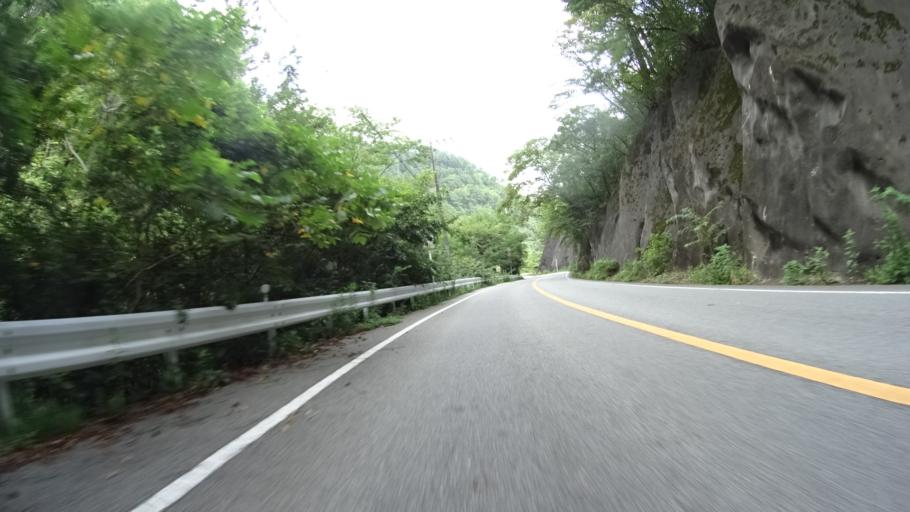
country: JP
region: Yamanashi
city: Kofu-shi
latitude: 35.7008
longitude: 138.5606
